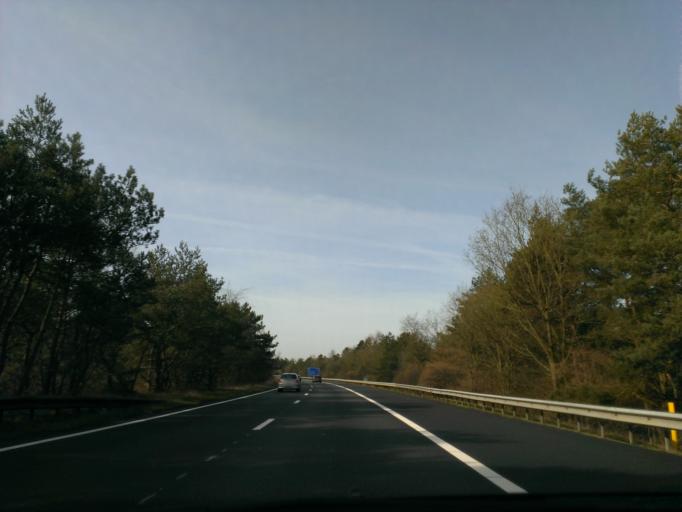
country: NL
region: Gelderland
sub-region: Gemeente Nunspeet
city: Nunspeet
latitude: 52.3842
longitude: 5.8314
